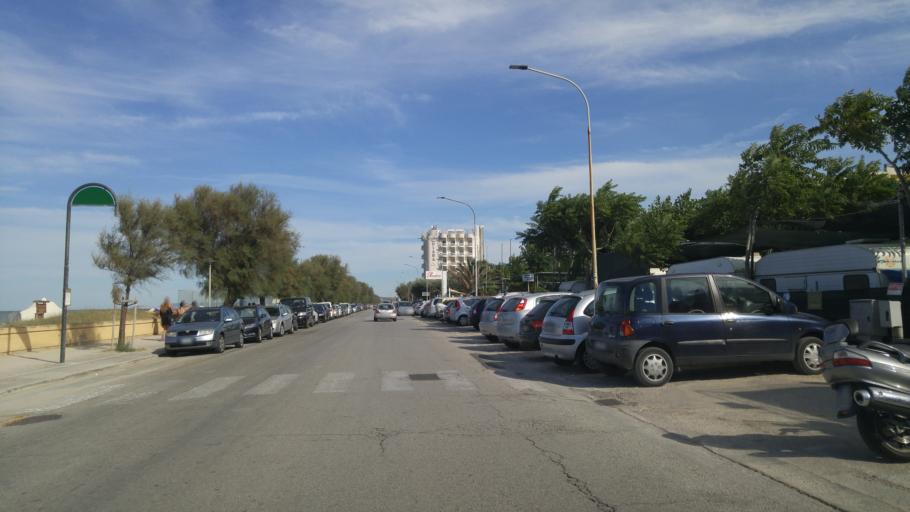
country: IT
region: The Marches
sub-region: Provincia di Ancona
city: Montignano-Marzocca
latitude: 43.6953
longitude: 13.2565
